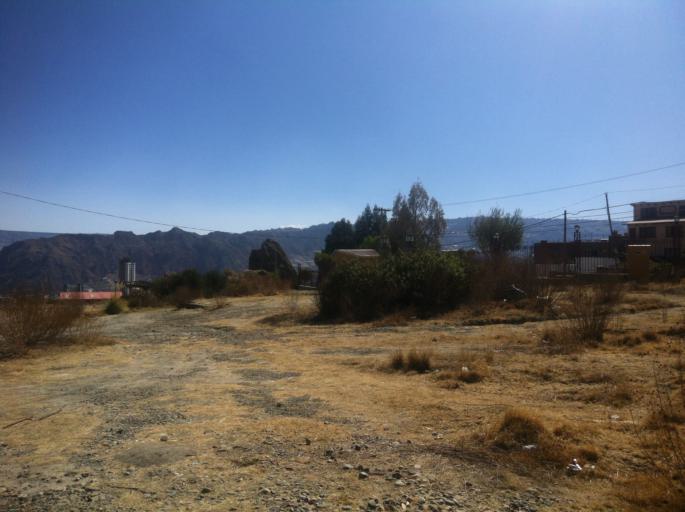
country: BO
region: La Paz
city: La Paz
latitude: -16.5350
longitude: -68.0668
